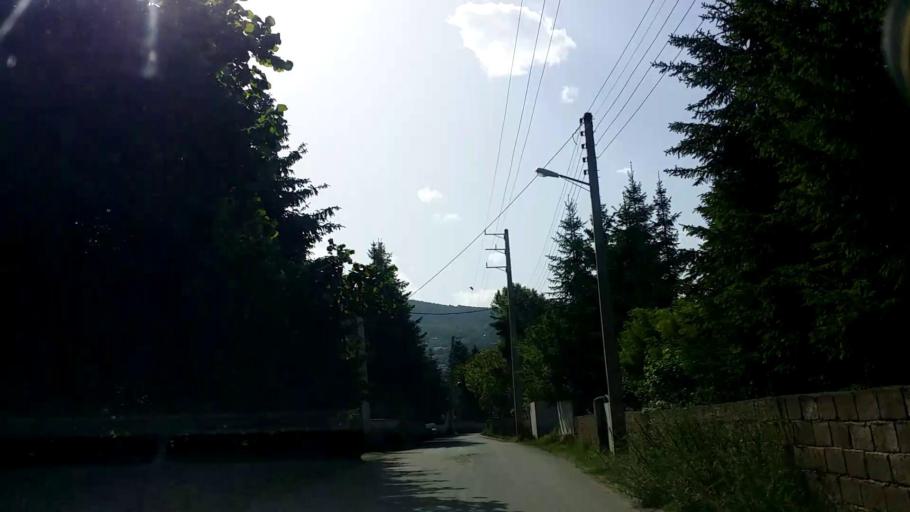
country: IR
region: Mazandaran
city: `Abbasabad
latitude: 36.5282
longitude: 51.1784
